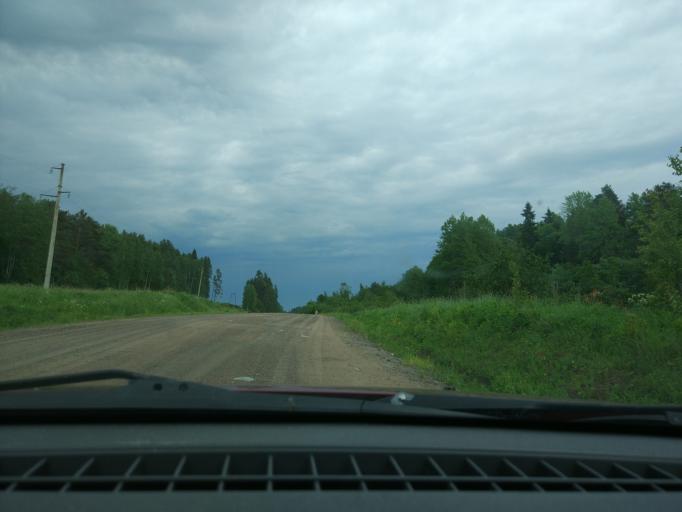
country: RU
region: Leningrad
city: Kuznechnoye
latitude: 61.2720
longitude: 29.8376
